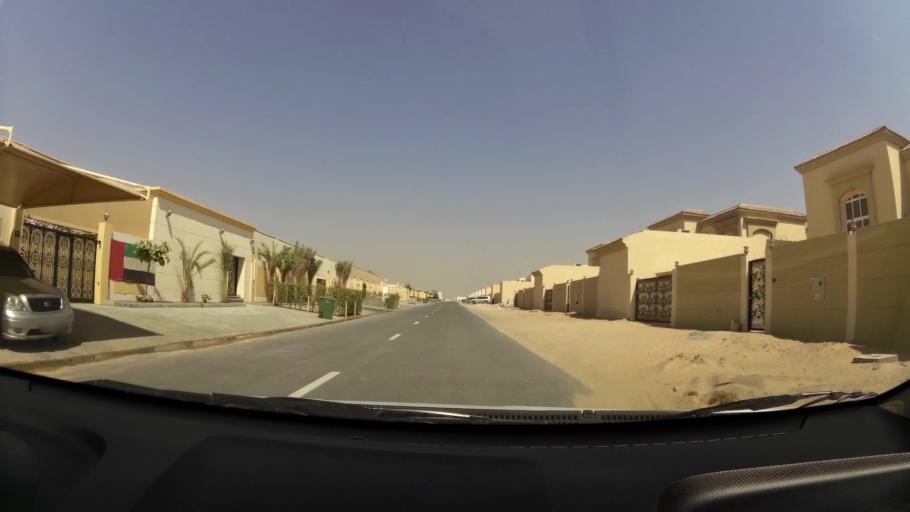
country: AE
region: Ajman
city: Ajman
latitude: 25.3989
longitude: 55.5482
